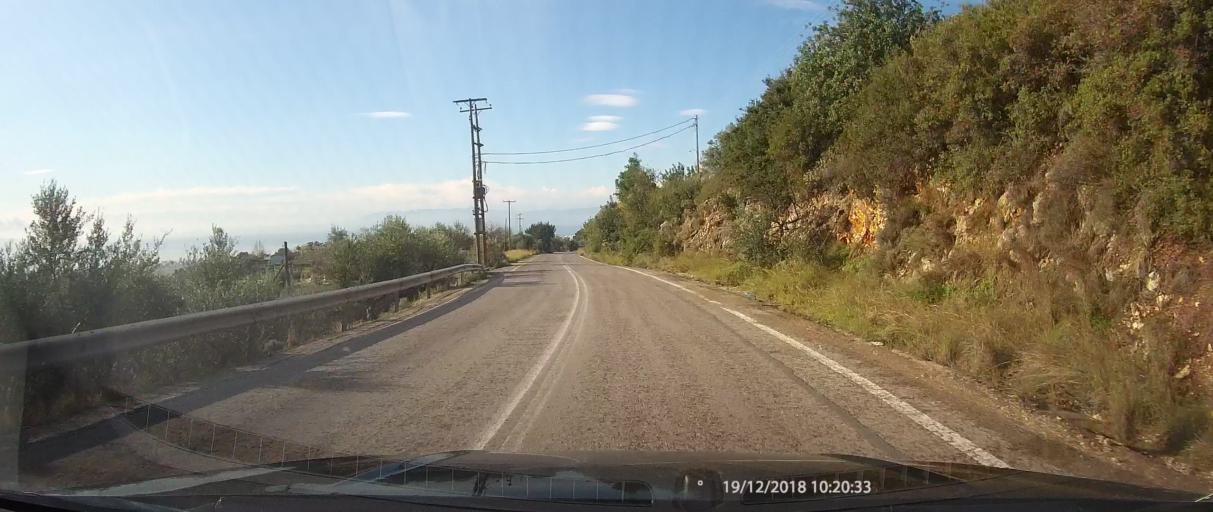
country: GR
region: Peloponnese
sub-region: Nomos Messinias
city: Kalamata
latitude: 37.0527
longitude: 22.1409
